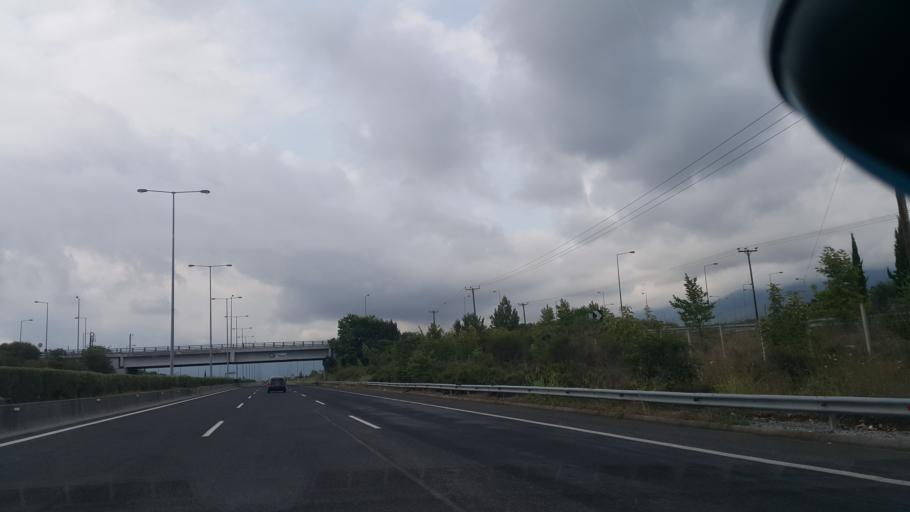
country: GR
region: Central Macedonia
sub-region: Nomos Pierias
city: Leptokarya
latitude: 40.1008
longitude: 22.5553
